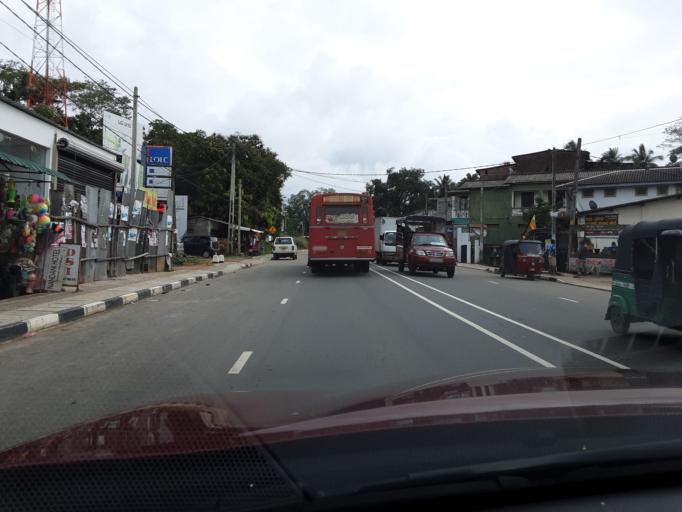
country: LK
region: Eastern Province
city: Ampara
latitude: 7.4031
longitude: 81.2435
